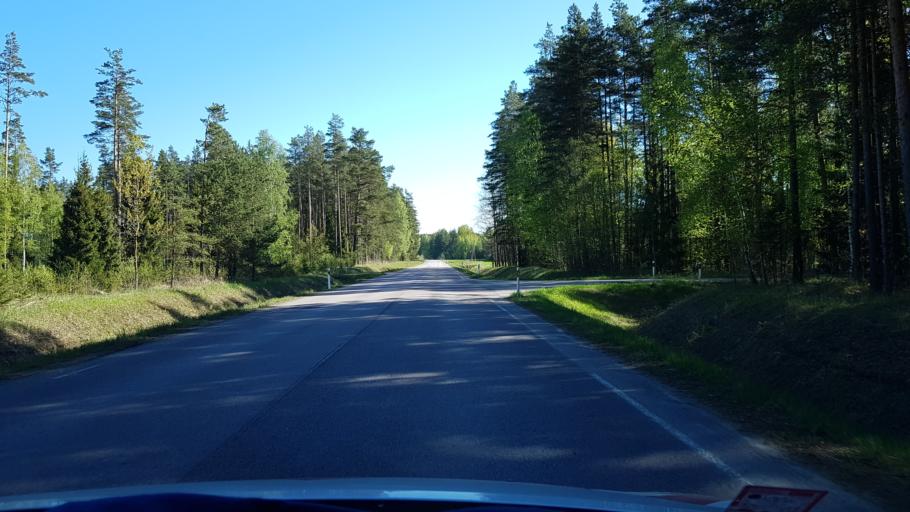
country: EE
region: Polvamaa
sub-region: Polva linn
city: Polva
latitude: 58.0999
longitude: 27.0993
